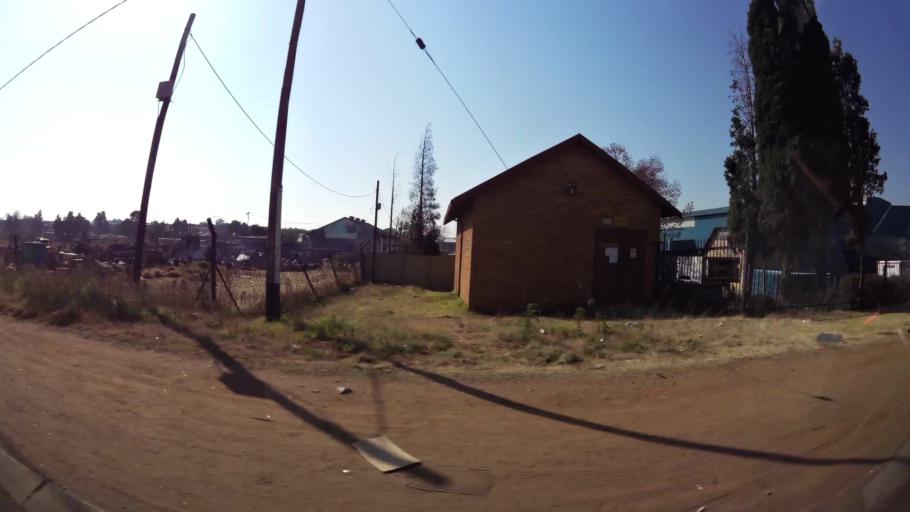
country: ZA
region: Gauteng
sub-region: Ekurhuleni Metropolitan Municipality
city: Boksburg
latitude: -26.1668
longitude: 28.2258
